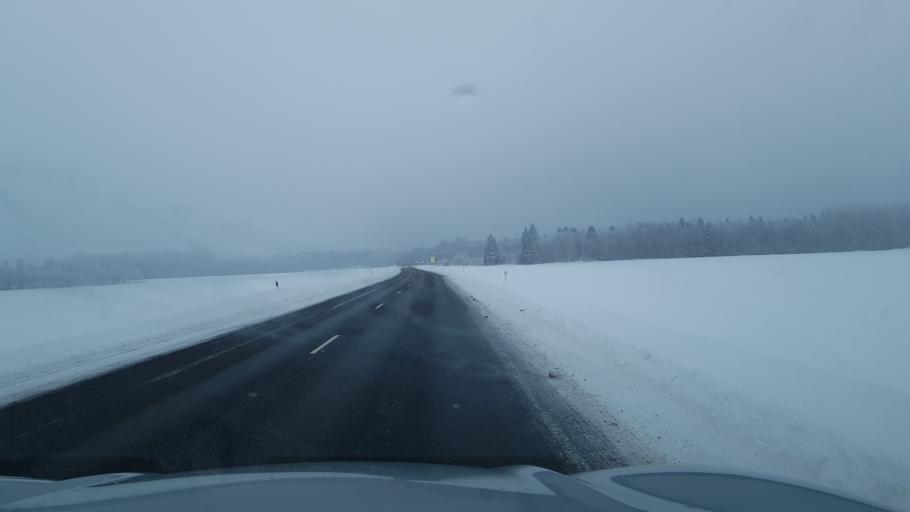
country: EE
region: Ida-Virumaa
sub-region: Johvi vald
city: Johvi
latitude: 59.3146
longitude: 27.3924
